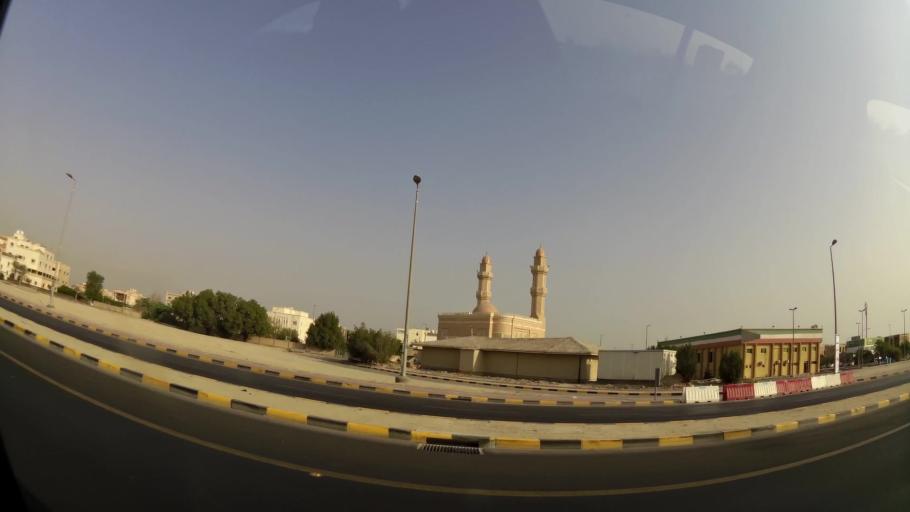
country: KW
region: Al Asimah
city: Ar Rabiyah
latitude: 29.3111
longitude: 47.8435
